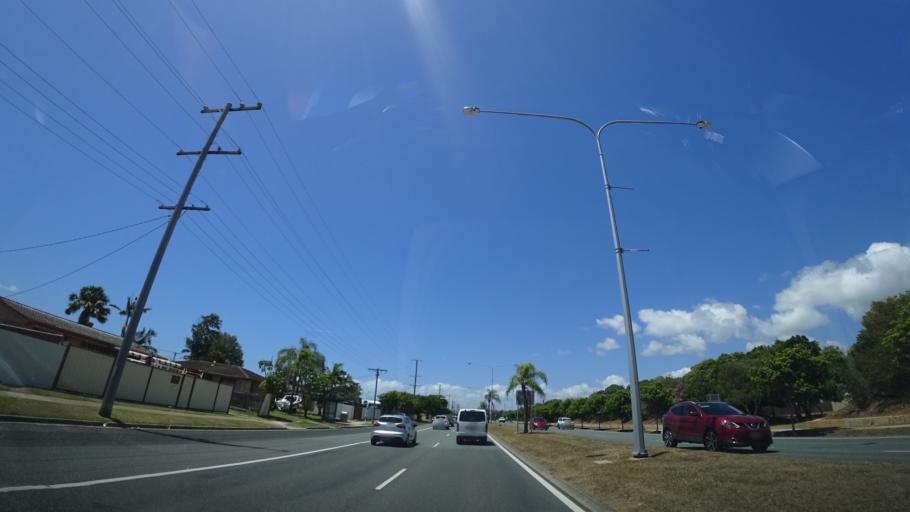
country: AU
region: Queensland
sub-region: Sunshine Coast
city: Mooloolaba
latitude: -26.7166
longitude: 153.1299
